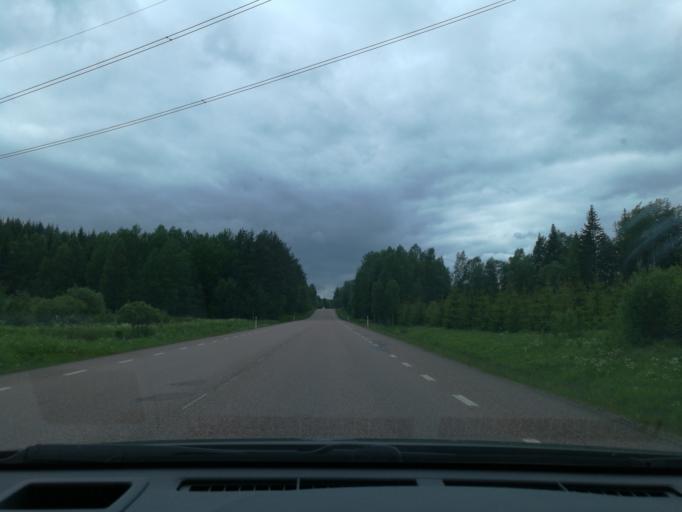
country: SE
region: Dalarna
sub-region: Smedjebackens Kommun
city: Smedjebacken
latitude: 60.1405
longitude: 15.3566
